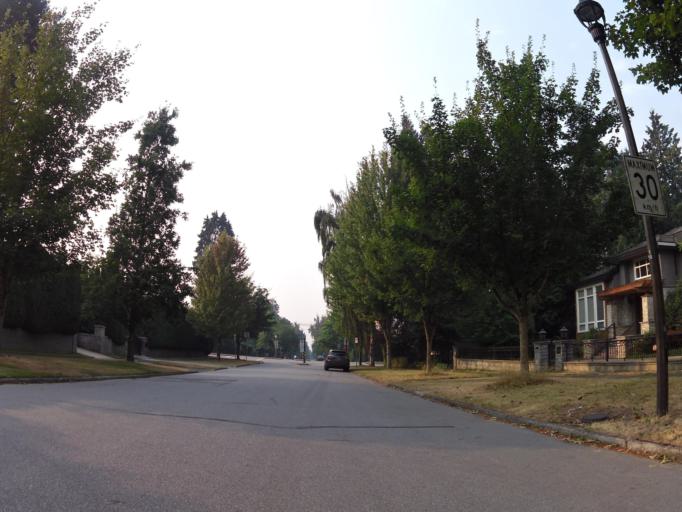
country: CA
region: British Columbia
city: Vancouver
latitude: 49.2352
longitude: -123.1477
